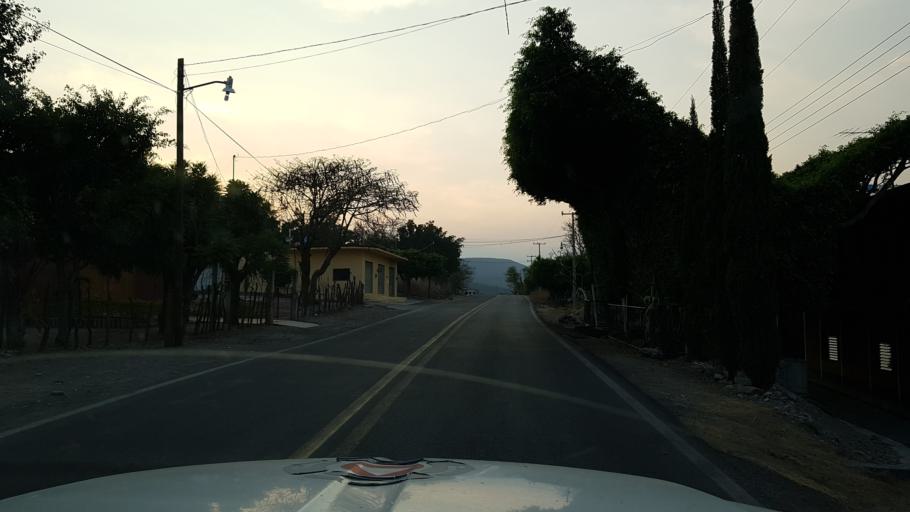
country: MX
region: Morelos
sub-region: Ayala
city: Abelardo L. Rodriguez
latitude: 18.7264
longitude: -98.9999
